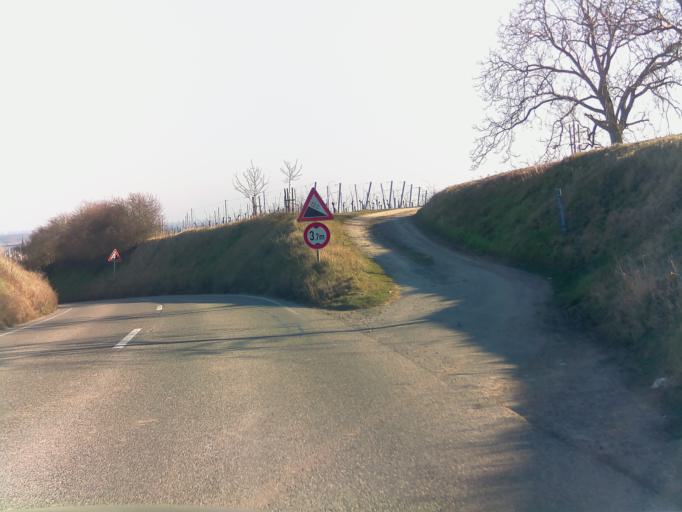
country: DE
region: Rheinland-Pfalz
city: Dackenheim
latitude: 49.5198
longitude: 8.1888
